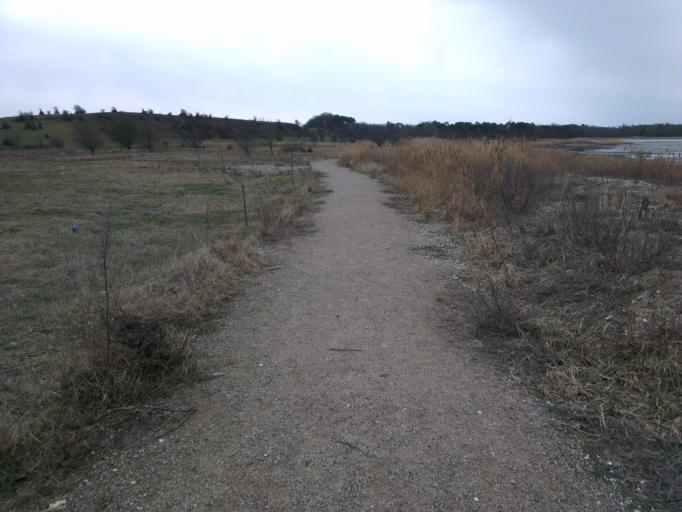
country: DK
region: Capital Region
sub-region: Frederikssund Kommune
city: Skibby
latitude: 55.8050
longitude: 11.8809
